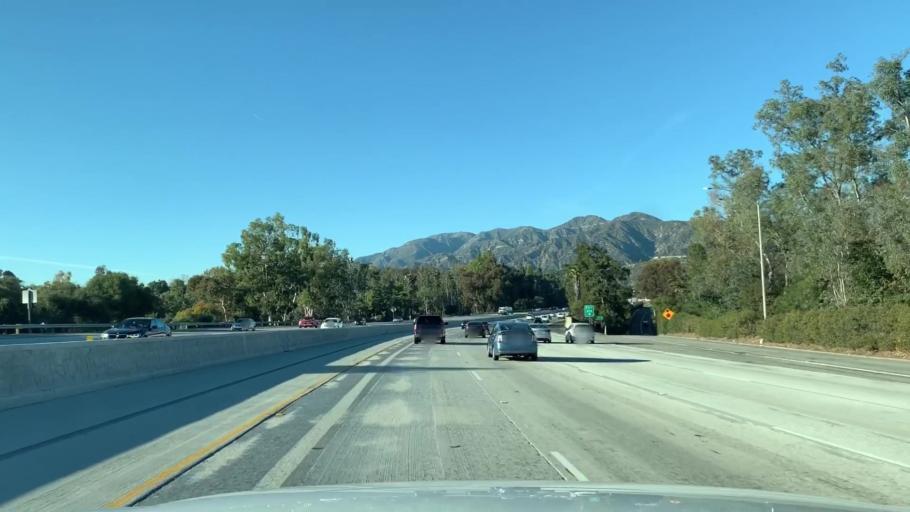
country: US
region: California
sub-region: Los Angeles County
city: La Canada Flintridge
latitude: 34.1874
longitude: -118.1796
